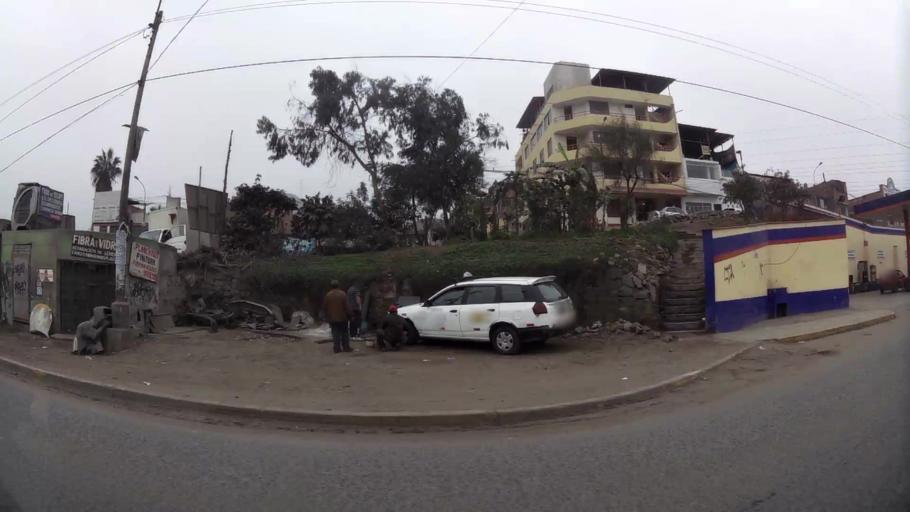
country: PE
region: Lima
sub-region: Lima
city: Surco
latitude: -12.1789
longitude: -76.9443
